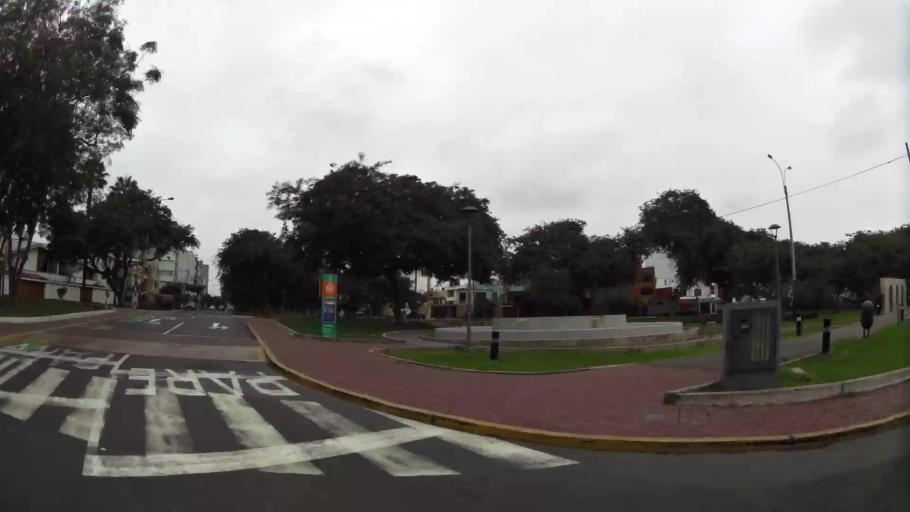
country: PE
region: Lima
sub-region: Lima
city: San Luis
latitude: -12.0926
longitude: -77.0191
